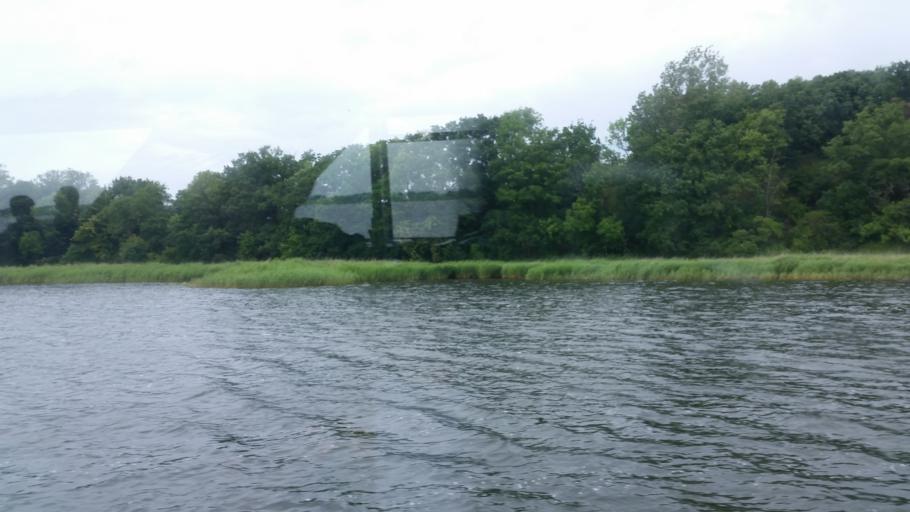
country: DE
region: Mecklenburg-Vorpommern
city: Hiddensee
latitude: 54.5838
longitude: 13.1170
